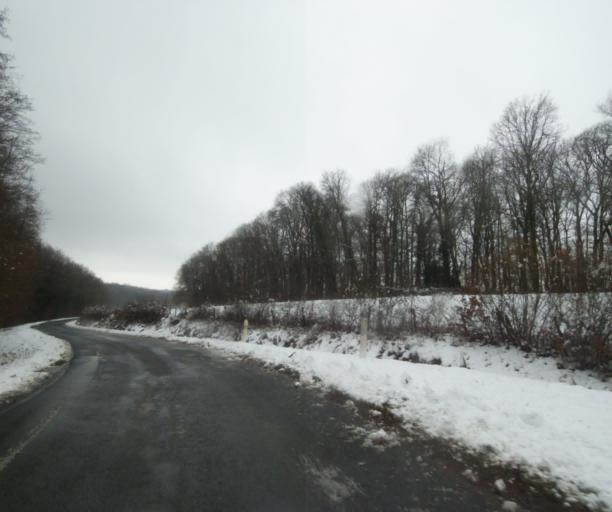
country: FR
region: Champagne-Ardenne
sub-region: Departement de la Haute-Marne
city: Laneuville-a-Remy
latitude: 48.4638
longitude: 4.8551
